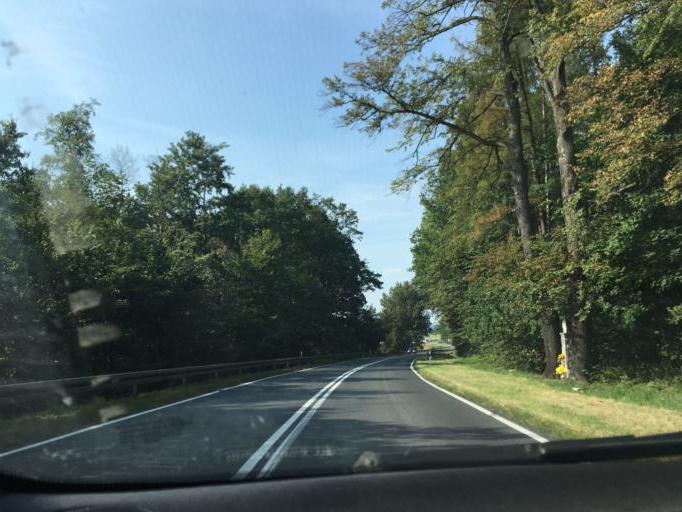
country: PL
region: Opole Voivodeship
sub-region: Powiat nyski
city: Nysa
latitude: 50.4355
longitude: 17.4085
